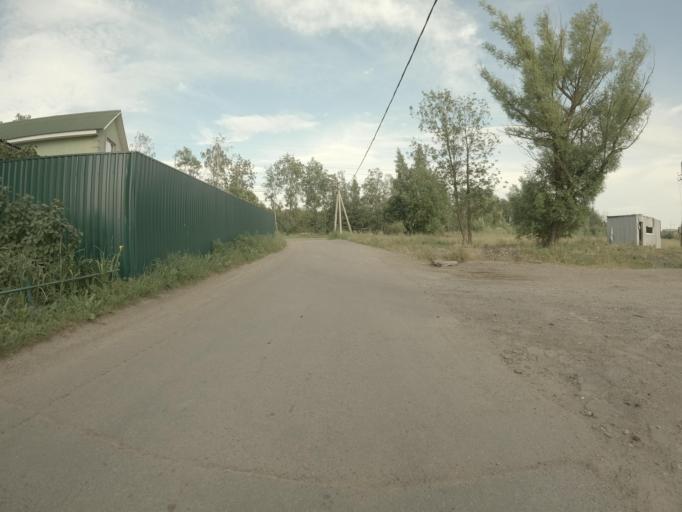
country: RU
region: St.-Petersburg
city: Krasnogvargeisky
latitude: 59.9355
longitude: 30.5197
